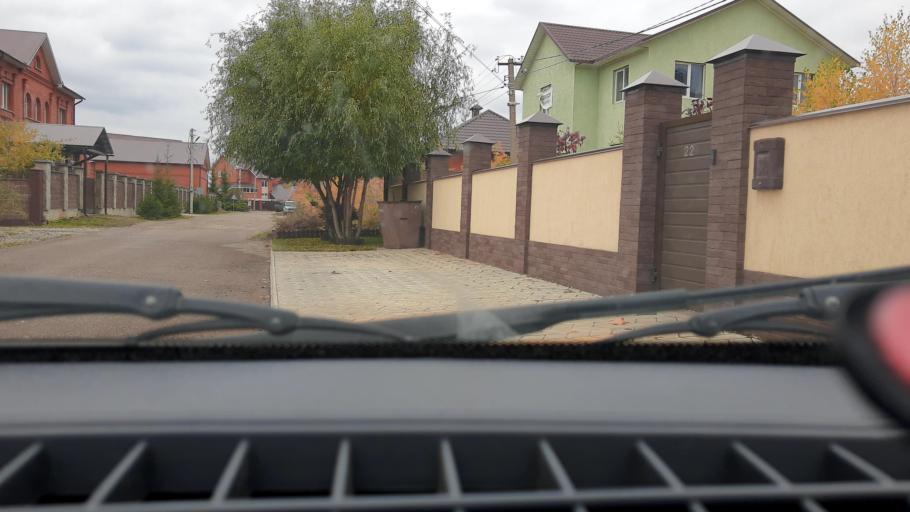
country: RU
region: Bashkortostan
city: Ufa
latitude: 54.7707
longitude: 55.9492
